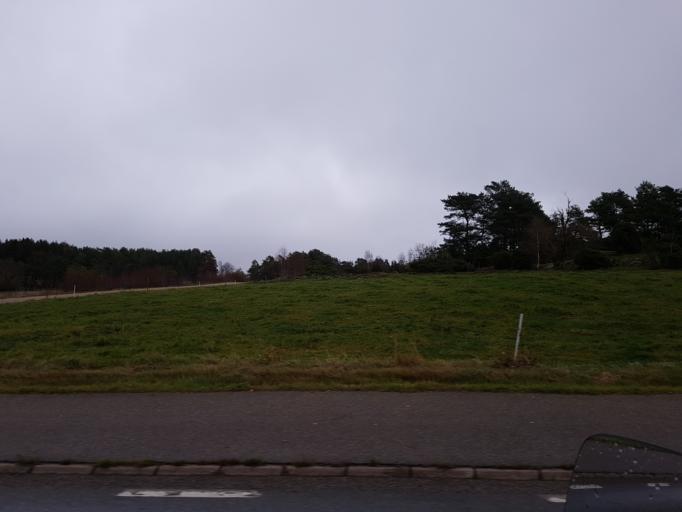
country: SE
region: Vaestra Goetaland
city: Svanesund
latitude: 58.1489
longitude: 11.8031
